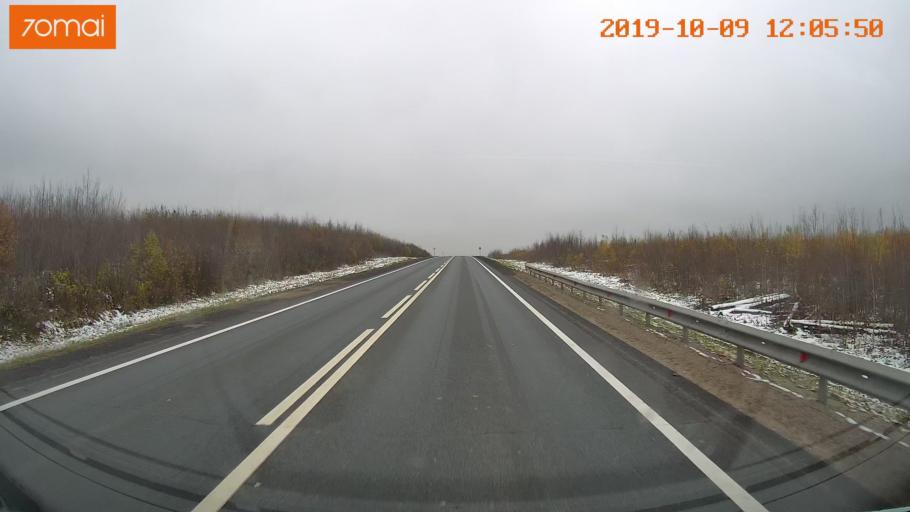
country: RU
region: Jaroslavl
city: Prechistoye
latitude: 58.6237
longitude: 40.3310
